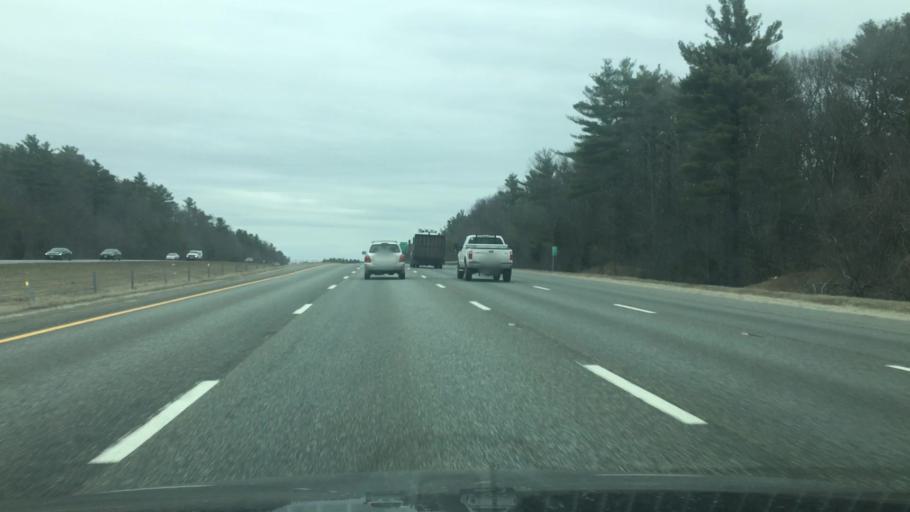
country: US
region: Massachusetts
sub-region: Essex County
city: Topsfield
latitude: 42.6303
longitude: -70.9778
